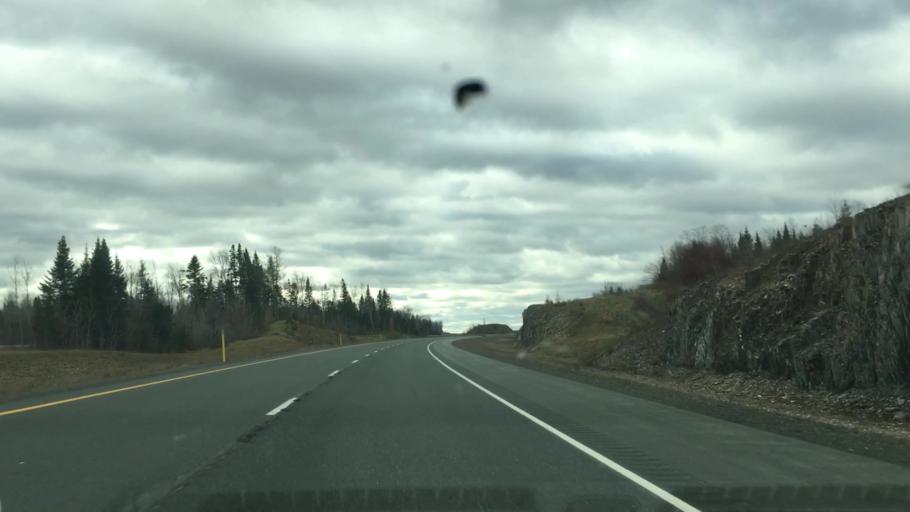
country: US
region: Maine
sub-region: Aroostook County
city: Easton
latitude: 46.6169
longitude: -67.7403
